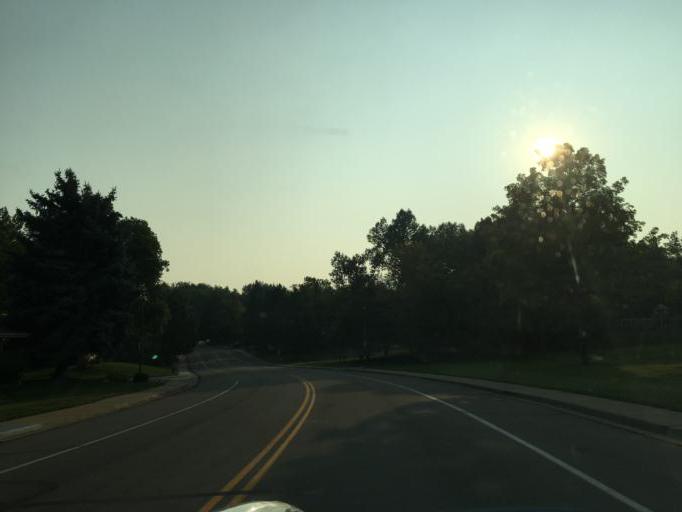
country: US
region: Colorado
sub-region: Adams County
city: Westminster
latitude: 39.8788
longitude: -105.0493
